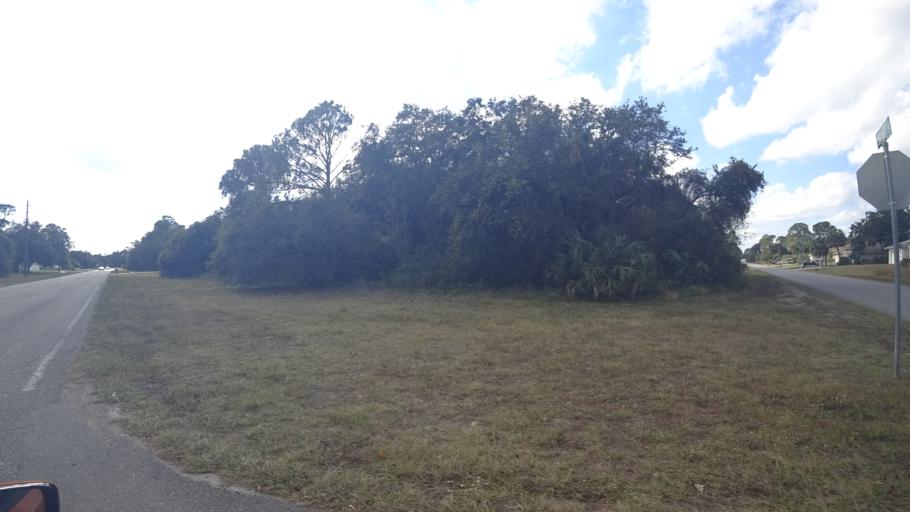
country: US
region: Florida
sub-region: Charlotte County
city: Port Charlotte
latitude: 27.0363
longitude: -82.1337
